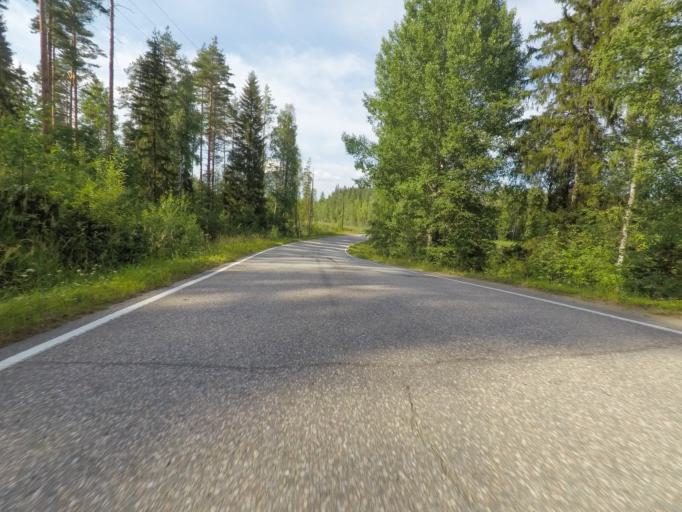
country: FI
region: Southern Savonia
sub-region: Savonlinna
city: Sulkava
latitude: 61.7815
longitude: 28.2397
